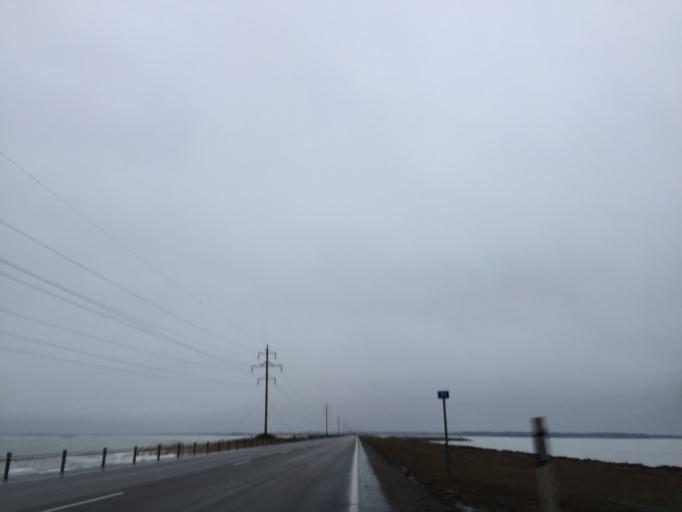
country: EE
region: Saare
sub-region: Orissaare vald
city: Orissaare
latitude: 58.5665
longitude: 23.1619
